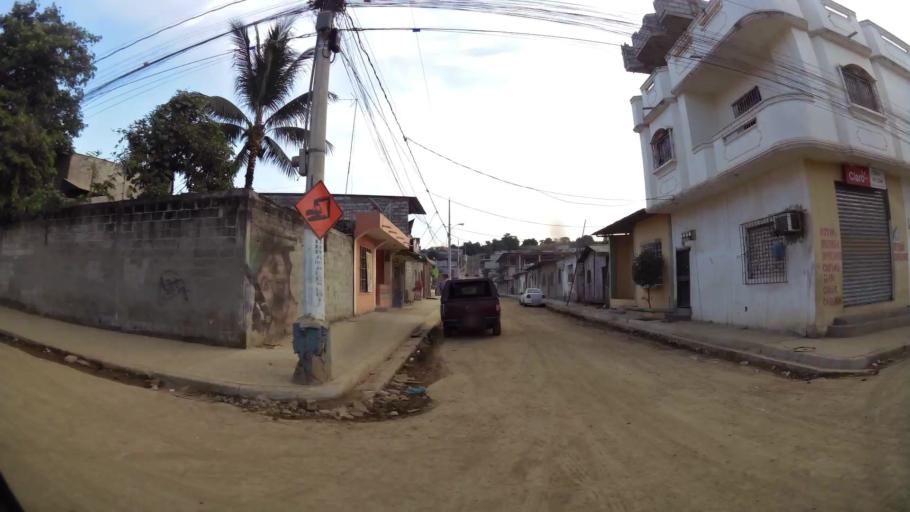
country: EC
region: Guayas
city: Eloy Alfaro
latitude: -2.0799
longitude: -79.8982
